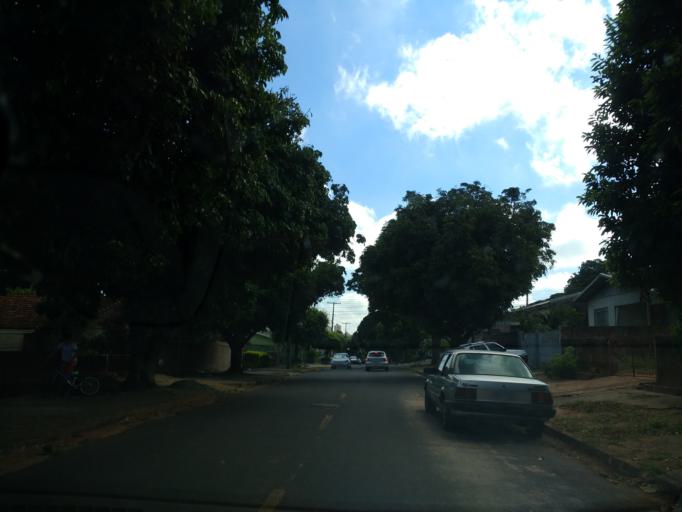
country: BR
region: Parana
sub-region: Umuarama
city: Umuarama
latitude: -23.7729
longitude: -53.3012
